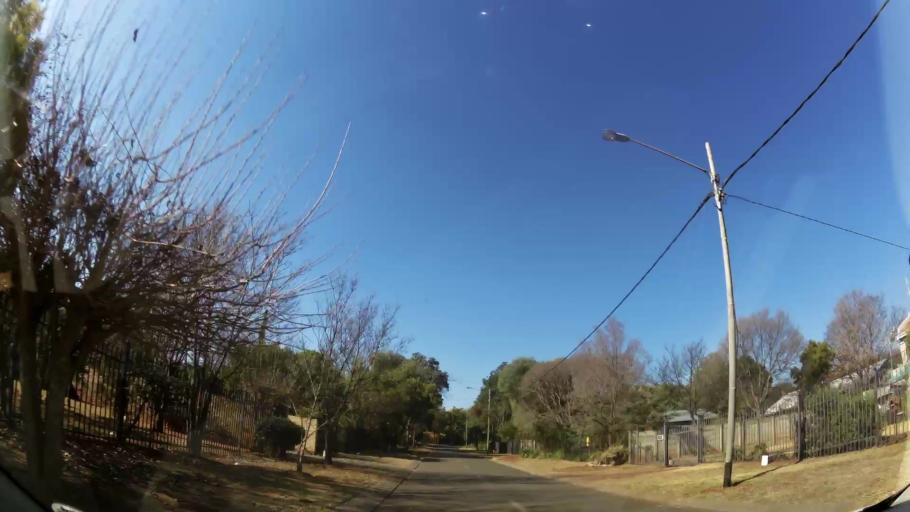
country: ZA
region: Gauteng
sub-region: City of Tshwane Metropolitan Municipality
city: Centurion
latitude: -25.8341
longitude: 28.1764
